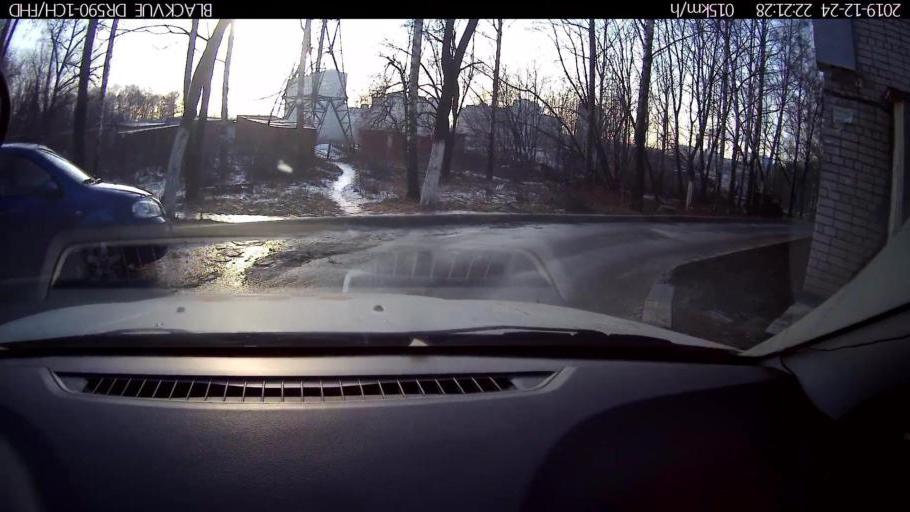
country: RU
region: Nizjnij Novgorod
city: Nizhniy Novgorod
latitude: 56.2369
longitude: 43.9707
